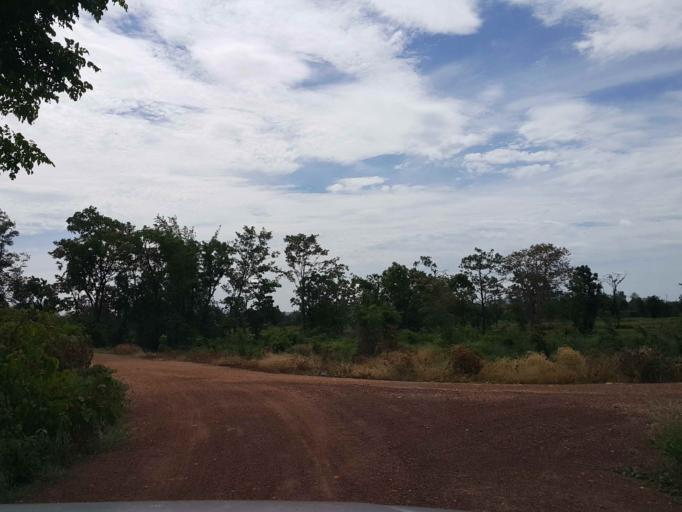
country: TH
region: Sukhothai
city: Ban Dan Lan Hoi
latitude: 17.0930
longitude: 99.4744
